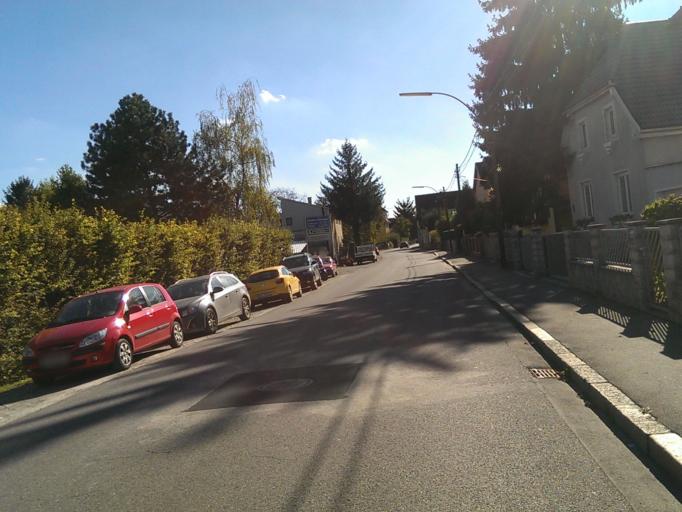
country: AT
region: Styria
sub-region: Politischer Bezirk Graz-Umgebung
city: Feldkirchen bei Graz
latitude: 47.0412
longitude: 15.4333
